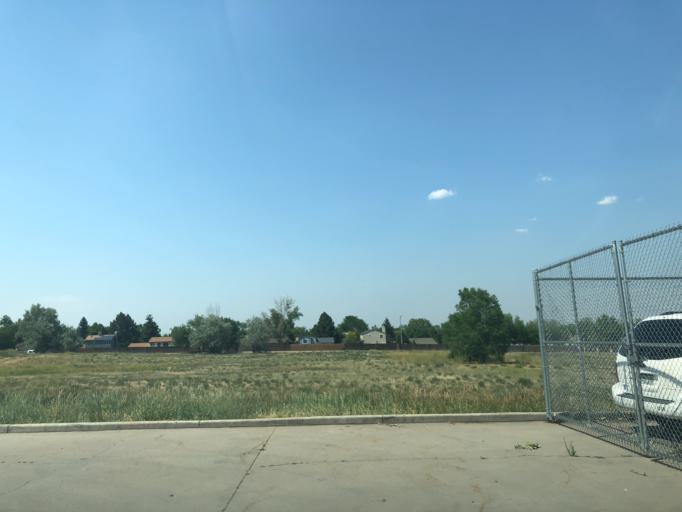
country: US
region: Colorado
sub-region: Arapahoe County
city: Dove Valley
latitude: 39.6372
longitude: -104.7864
